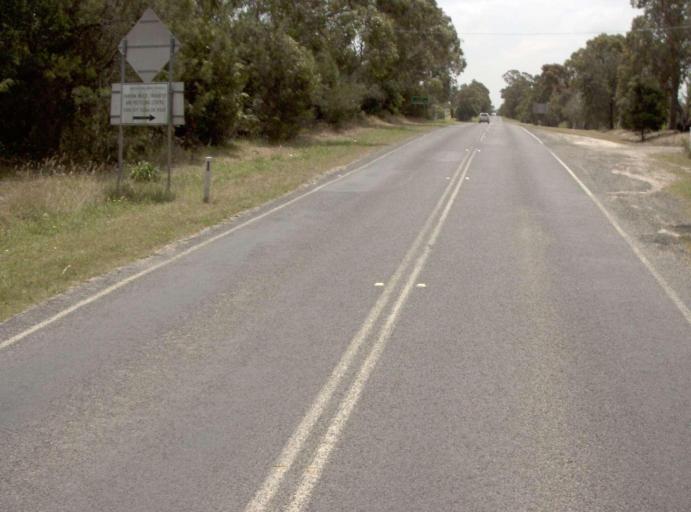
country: AU
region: Victoria
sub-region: Latrobe
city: Traralgon
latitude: -38.5446
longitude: 146.7018
